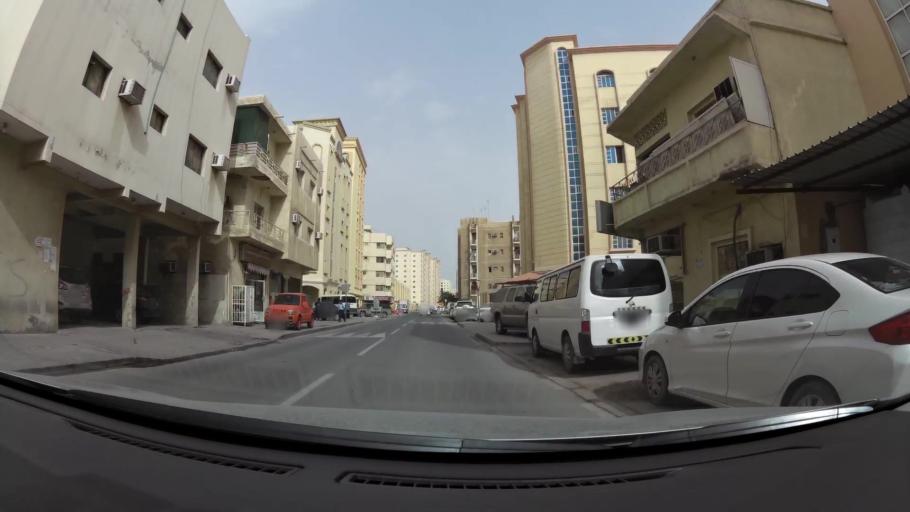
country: QA
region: Baladiyat ad Dawhah
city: Doha
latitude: 25.2752
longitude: 51.5455
